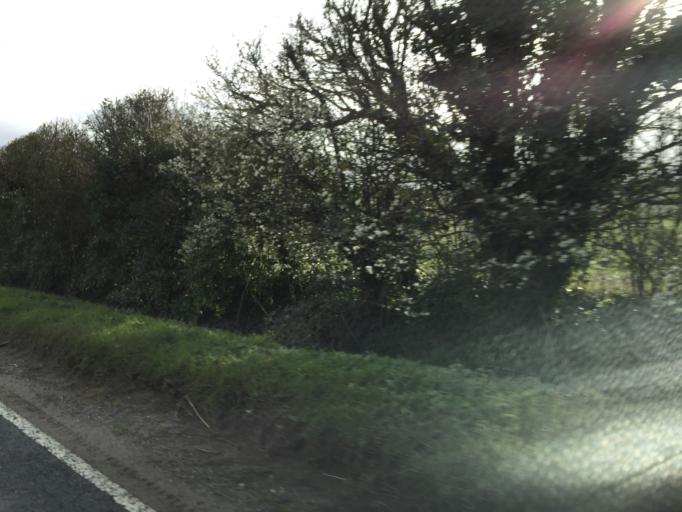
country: GB
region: England
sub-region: Oxfordshire
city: Cholsey
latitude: 51.5534
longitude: -1.1798
